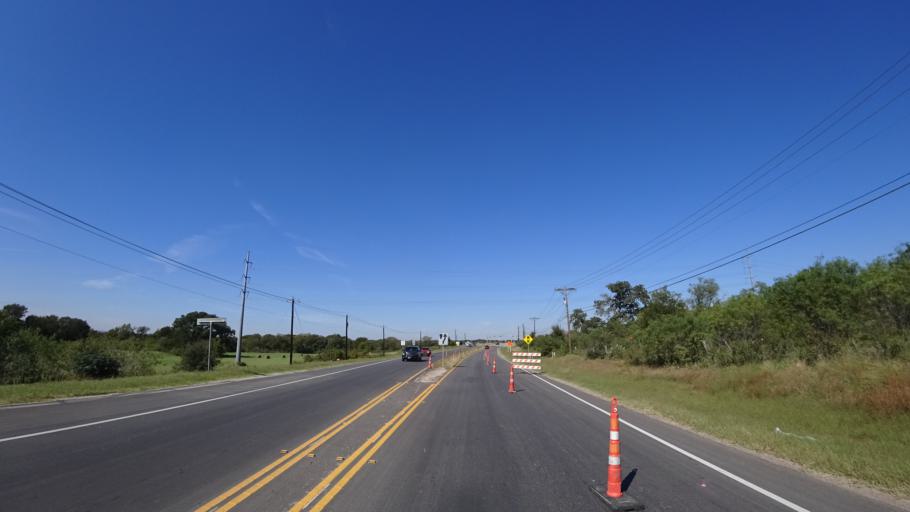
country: US
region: Texas
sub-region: Travis County
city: Hornsby Bend
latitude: 30.2553
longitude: -97.6088
